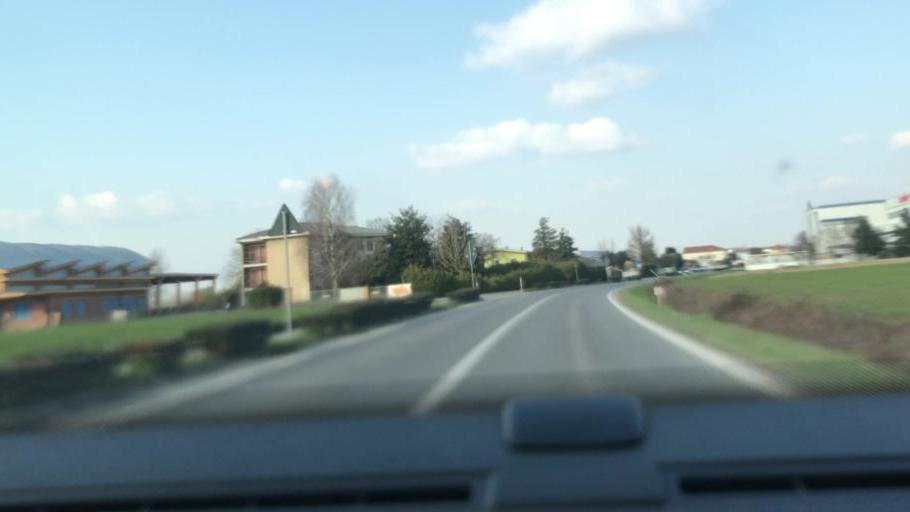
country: IT
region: Lombardy
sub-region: Provincia di Cremona
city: Vicomoscano
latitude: 44.9539
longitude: 10.4717
